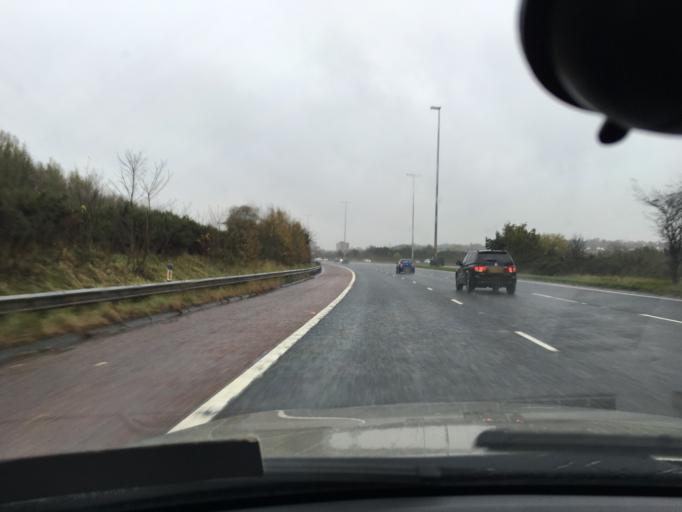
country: GB
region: Northern Ireland
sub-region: Newtownabbey District
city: Newtownabbey
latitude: 54.6415
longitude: -5.9170
